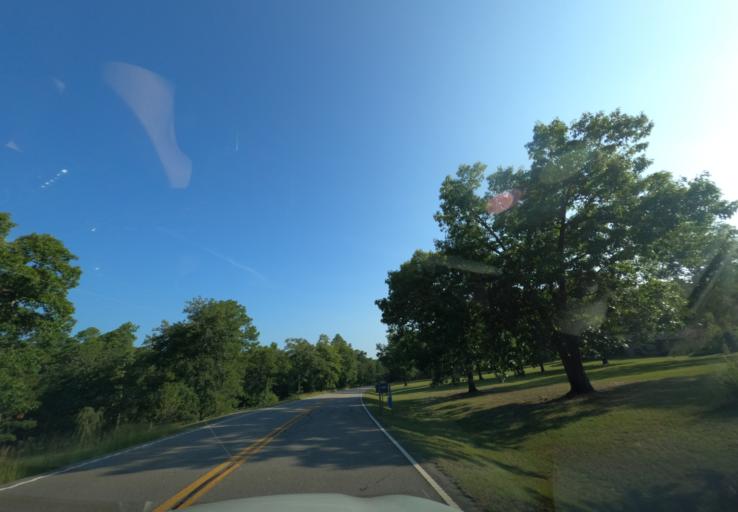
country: US
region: South Carolina
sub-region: Edgefield County
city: Murphys Estates
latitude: 33.5885
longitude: -81.9793
